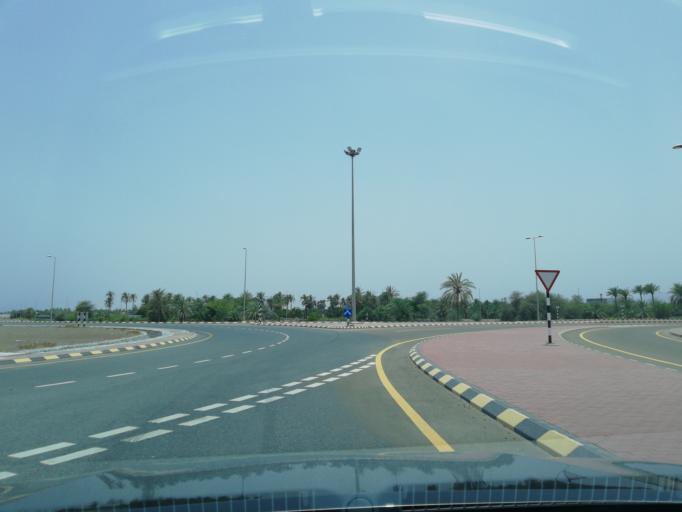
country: OM
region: Al Batinah
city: Shinas
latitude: 24.8100
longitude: 56.4455
